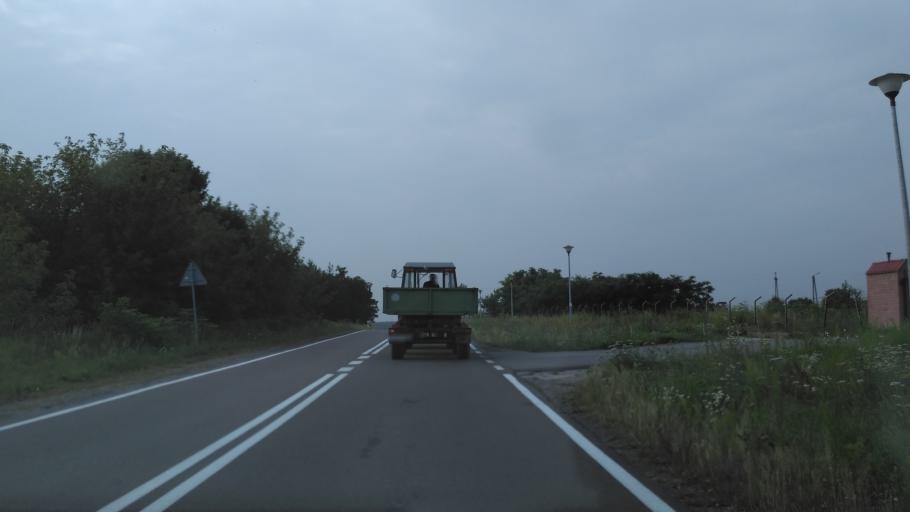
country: PL
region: Lublin Voivodeship
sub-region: Powiat chelmski
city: Rejowiec Fabryczny
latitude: 51.1814
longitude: 23.1749
